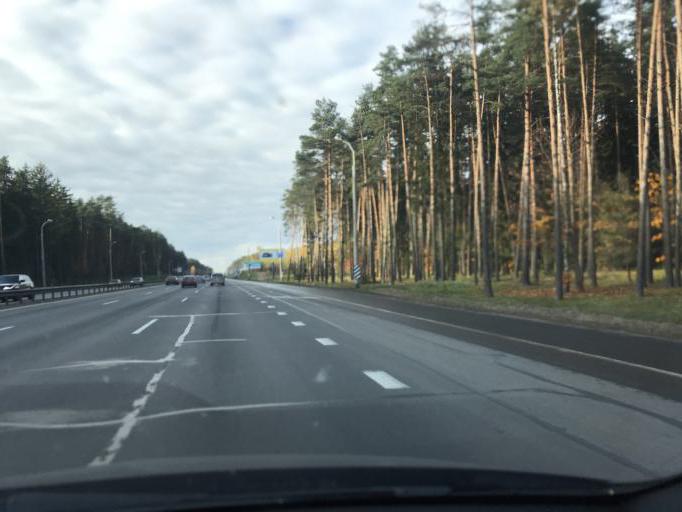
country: BY
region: Minsk
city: Borovlyany
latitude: 53.9488
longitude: 27.6577
